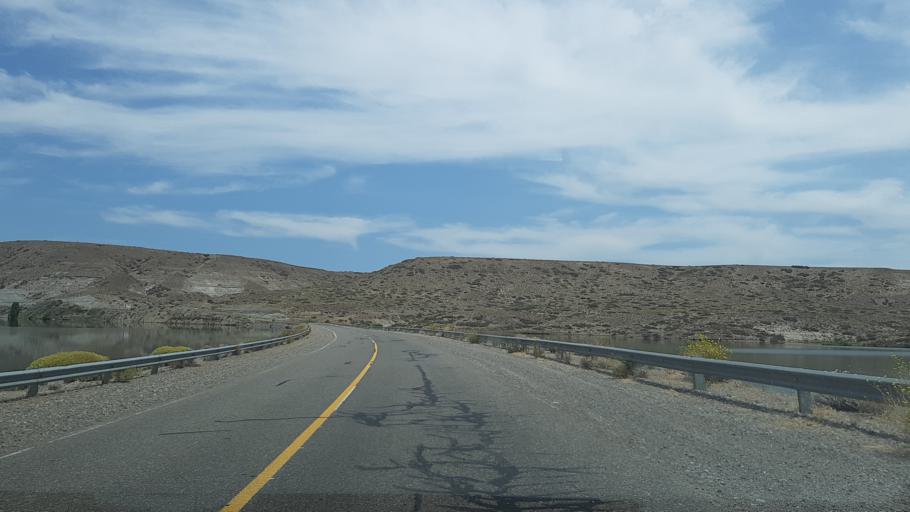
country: AR
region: Neuquen
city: Junin de los Andes
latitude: -40.4376
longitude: -70.6546
